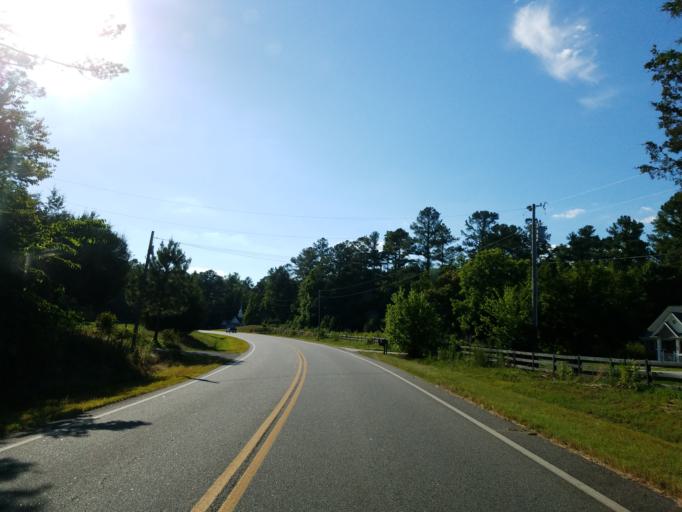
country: US
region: Georgia
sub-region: Gordon County
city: Calhoun
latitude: 34.6075
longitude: -85.0400
